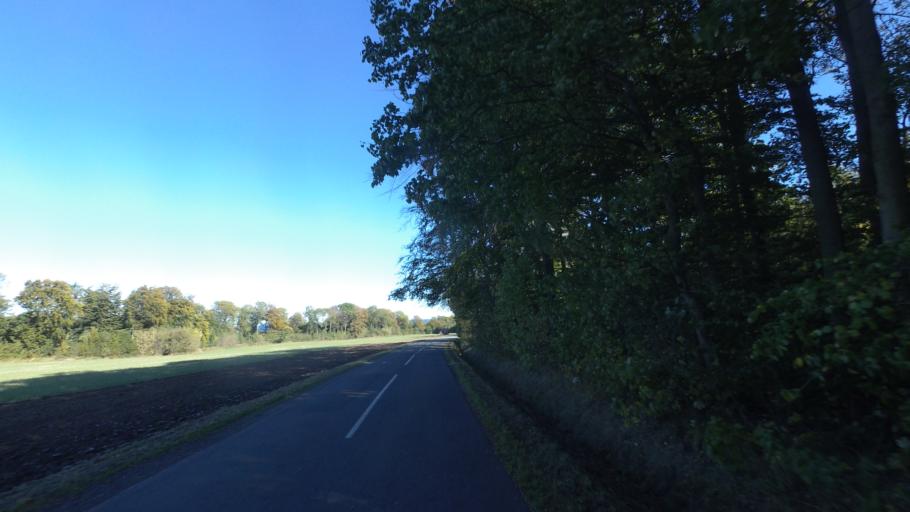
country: DK
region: Capital Region
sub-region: Bornholm Kommune
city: Nexo
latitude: 55.1109
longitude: 15.1235
